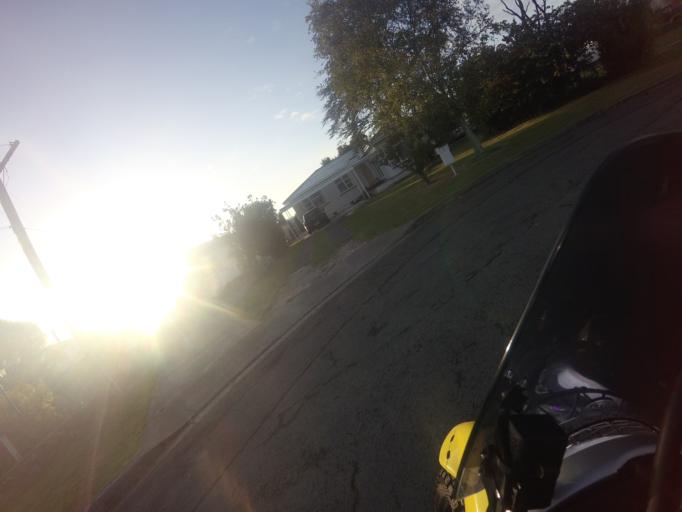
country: NZ
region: Gisborne
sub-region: Gisborne District
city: Gisborne
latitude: -38.6710
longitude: 178.0389
